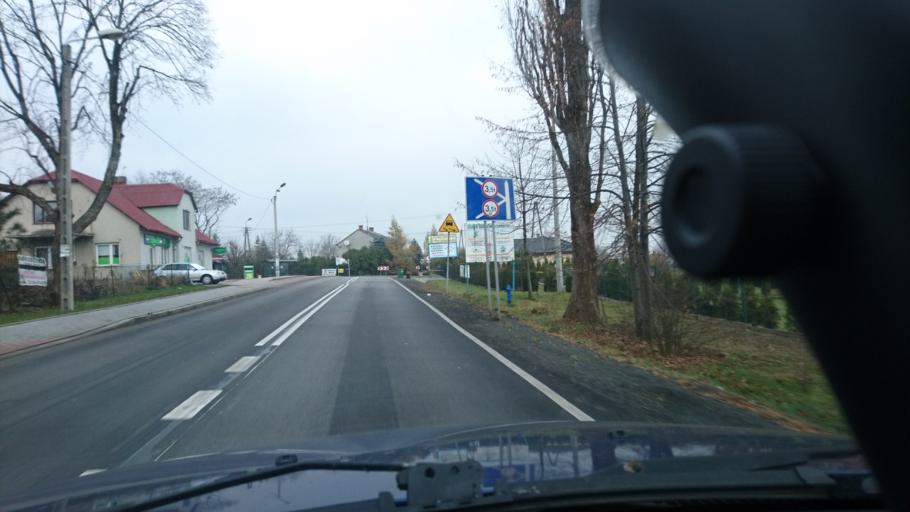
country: PL
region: Silesian Voivodeship
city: Janowice
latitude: 49.8669
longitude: 19.1165
